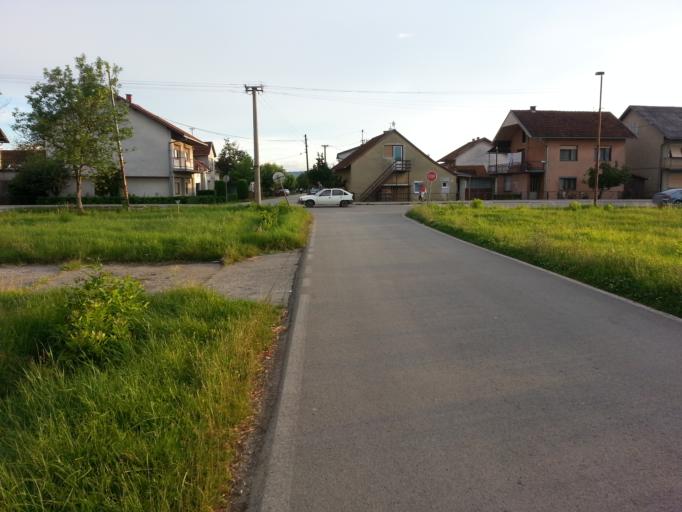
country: BA
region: Republika Srpska
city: Prijedor
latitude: 44.9827
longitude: 16.7288
